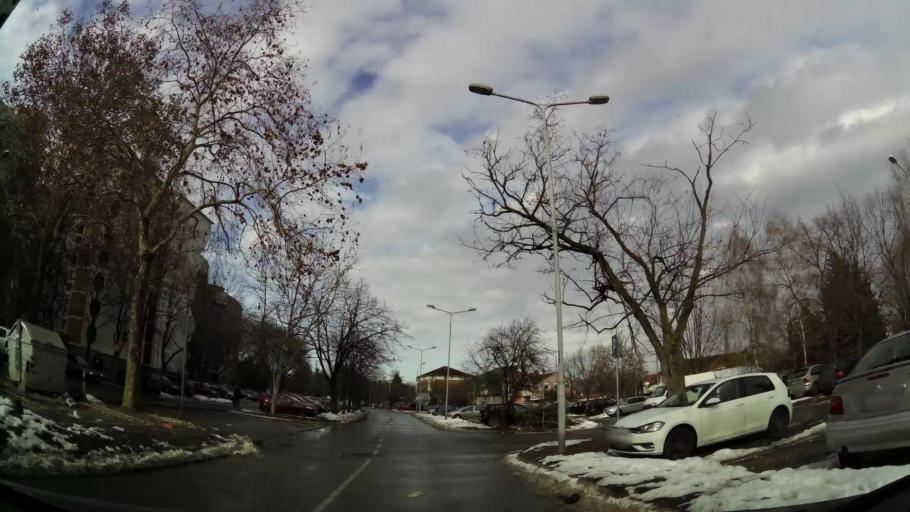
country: RS
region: Central Serbia
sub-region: Belgrade
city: Rakovica
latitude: 44.7395
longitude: 20.4262
